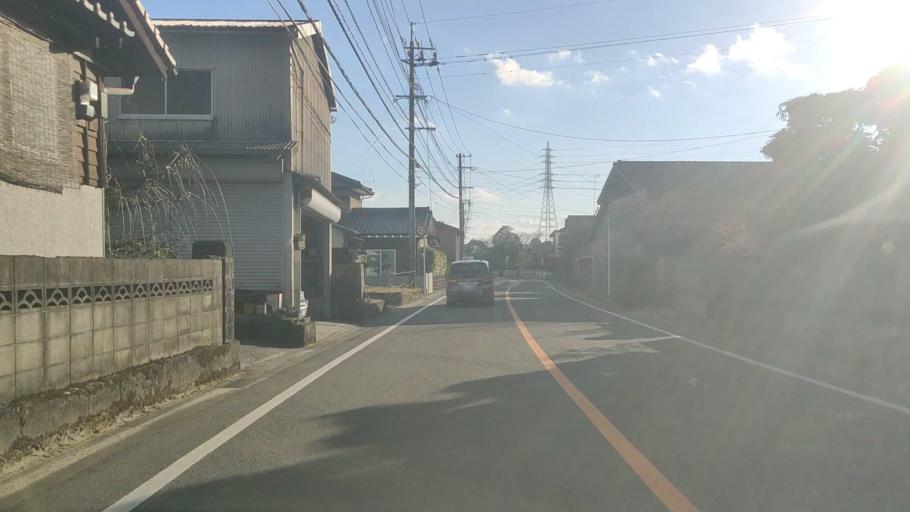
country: JP
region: Saga Prefecture
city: Saga-shi
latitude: 33.3229
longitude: 130.2679
